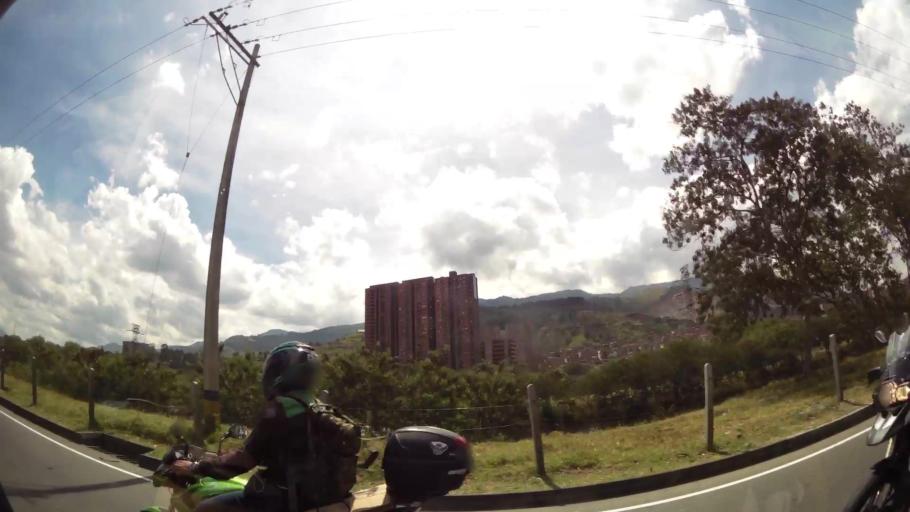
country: CO
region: Antioquia
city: Bello
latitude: 6.3273
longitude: -75.5524
